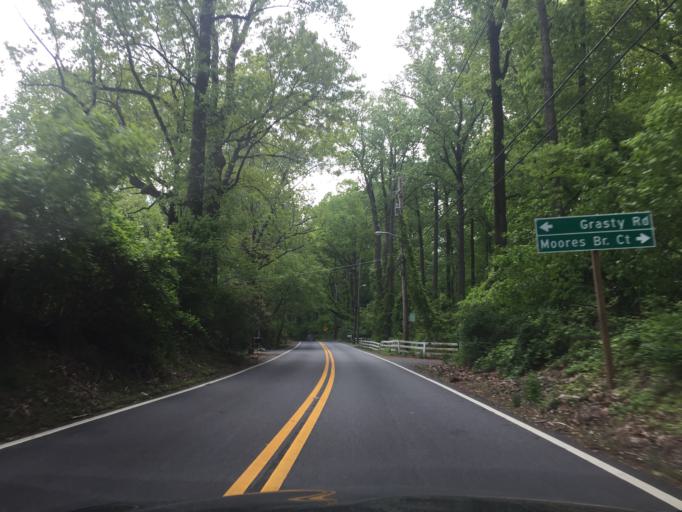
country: US
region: Maryland
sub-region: Baltimore County
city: Pikesville
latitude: 39.3947
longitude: -76.6816
